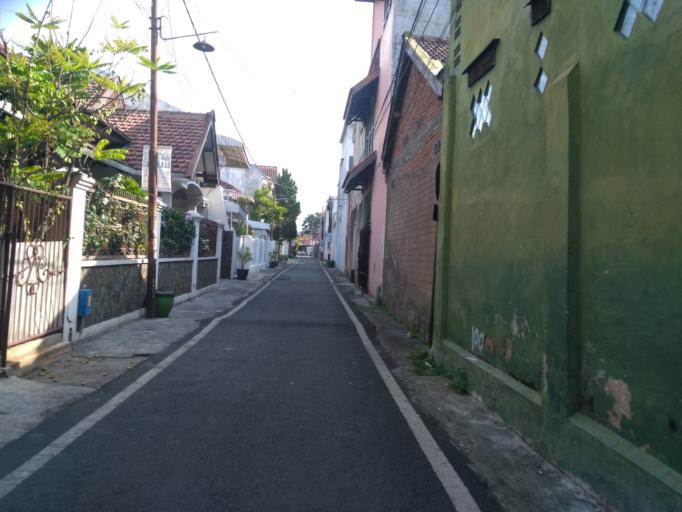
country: ID
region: East Java
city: Malang
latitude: -7.9393
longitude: 112.6094
